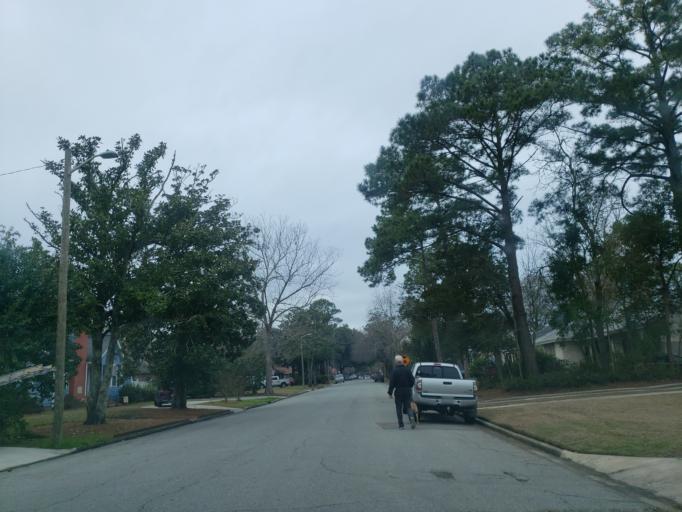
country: US
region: Georgia
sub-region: Chatham County
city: Savannah
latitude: 32.0400
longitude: -81.0956
